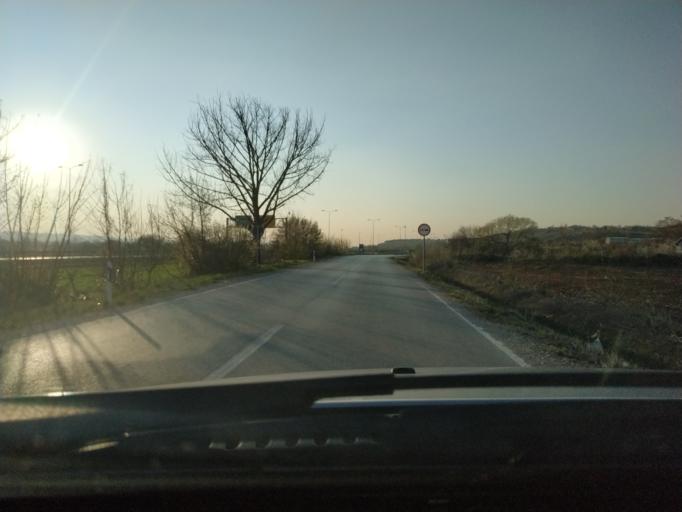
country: RS
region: Central Serbia
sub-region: Nisavski Okrug
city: Aleksinac
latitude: 43.5204
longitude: 21.7342
